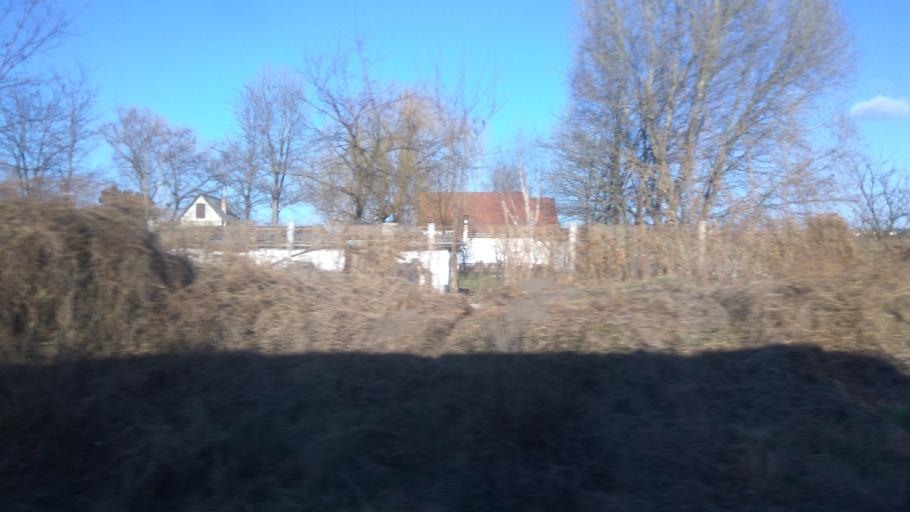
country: HU
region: Pest
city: Pecel
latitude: 47.4953
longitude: 19.3150
